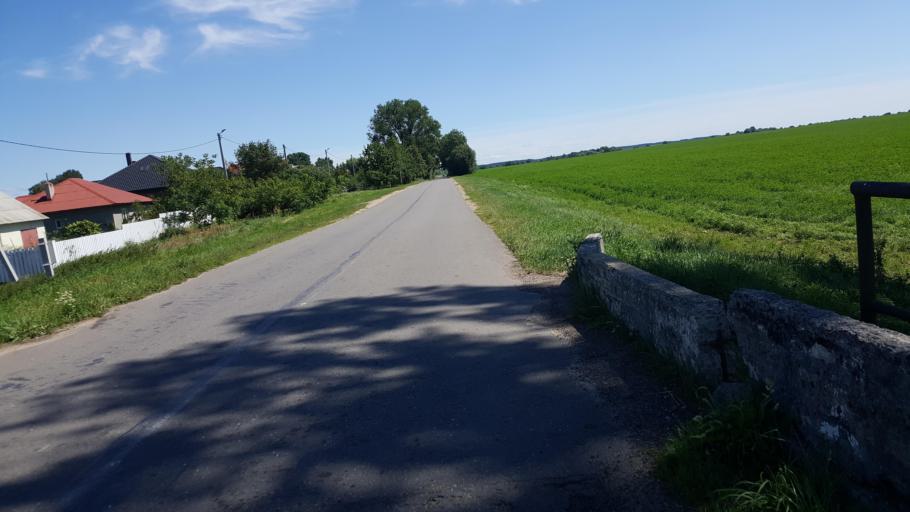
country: BY
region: Brest
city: Charnawchytsy
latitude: 52.2200
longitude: 23.7555
